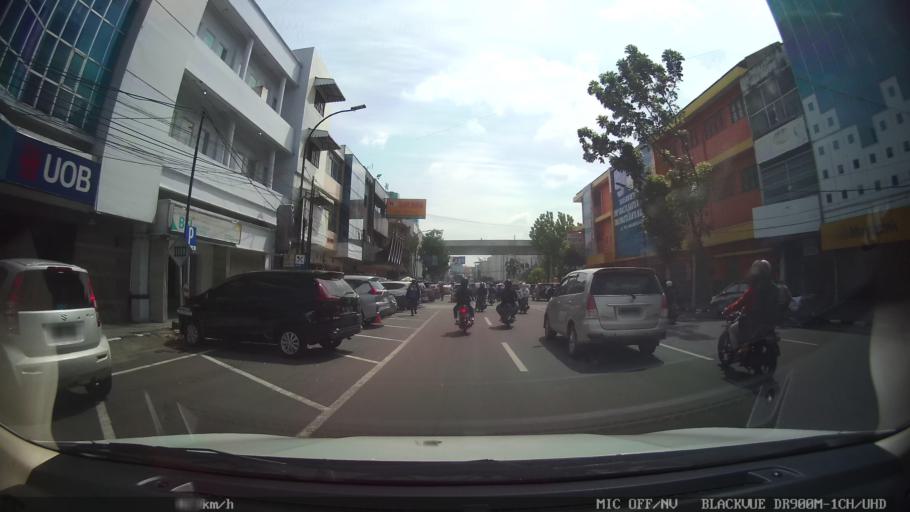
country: ID
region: North Sumatra
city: Medan
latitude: 3.5849
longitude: 98.6810
